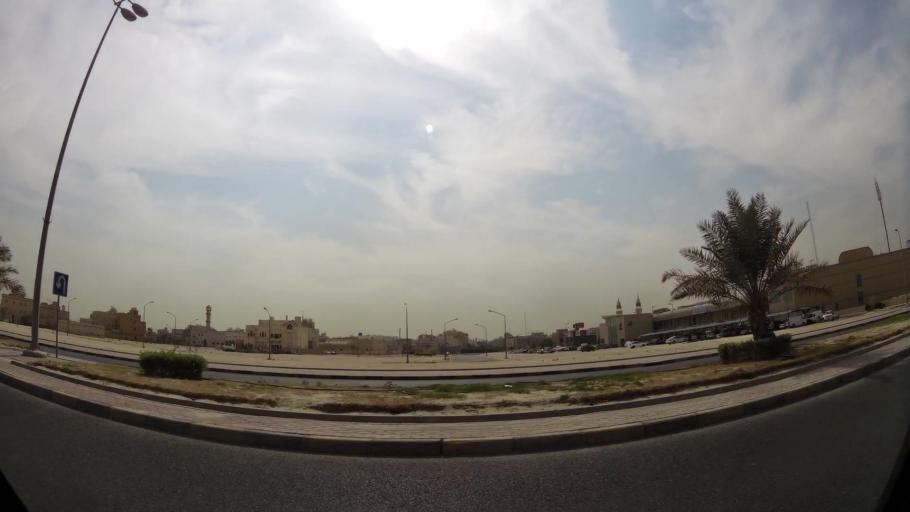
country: KW
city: Bayan
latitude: 29.2980
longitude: 48.0109
